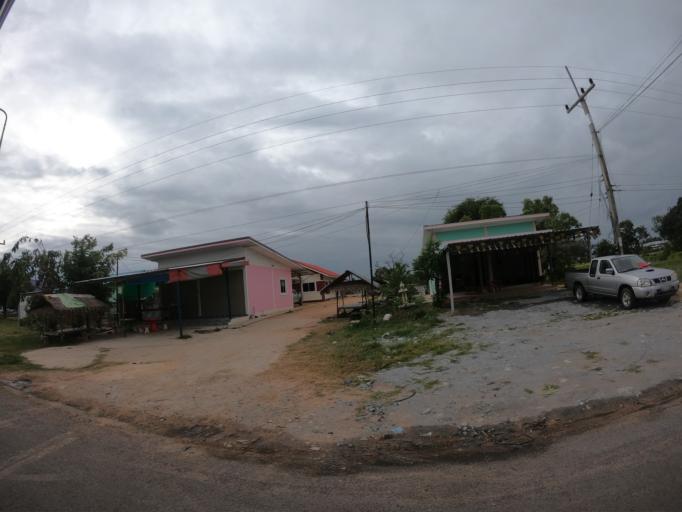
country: TH
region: Roi Et
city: Roi Et
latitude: 16.0815
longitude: 103.7054
